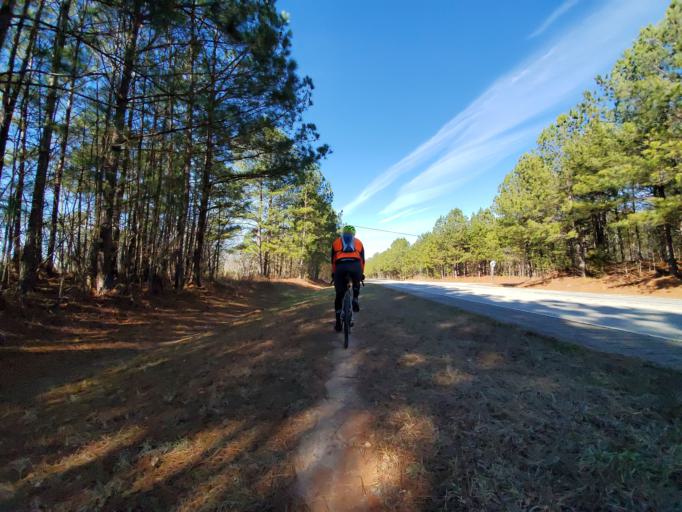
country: US
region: Georgia
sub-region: Fulton County
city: Chattahoochee Hills
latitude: 33.5763
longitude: -84.7991
